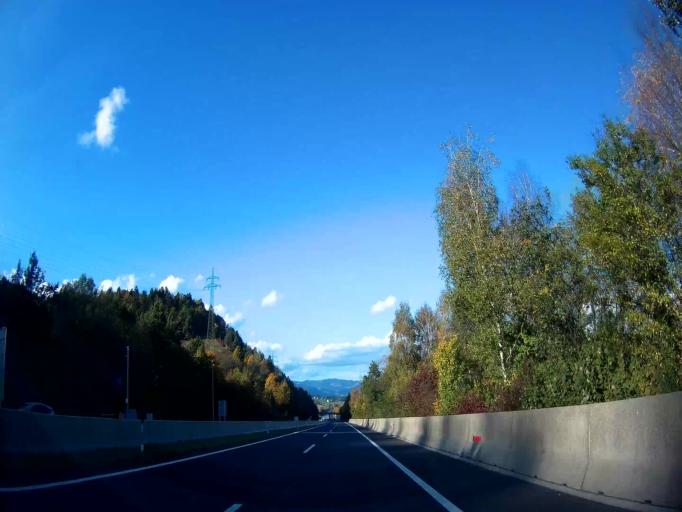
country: AT
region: Carinthia
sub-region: Politischer Bezirk Wolfsberg
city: Sankt Andrae
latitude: 46.7592
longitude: 14.8154
